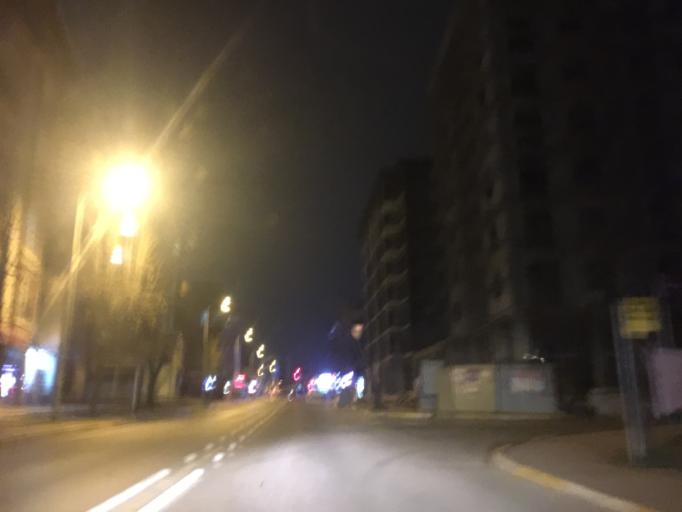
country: TR
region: Istanbul
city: Icmeler
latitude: 40.8242
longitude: 29.3102
